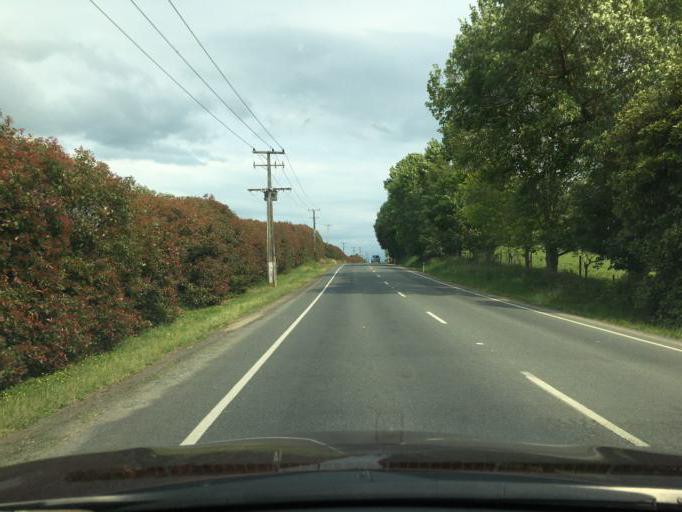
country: NZ
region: Waikato
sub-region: Waipa District
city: Cambridge
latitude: -38.0086
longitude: 175.3535
